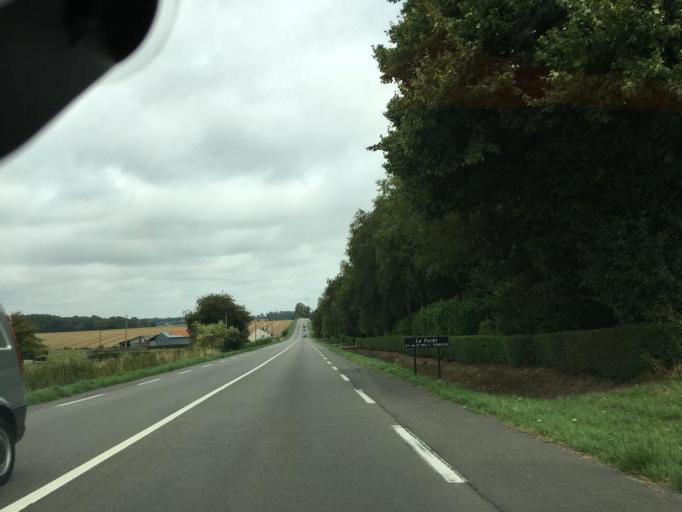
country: FR
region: Nord-Pas-de-Calais
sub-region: Departement du Pas-de-Calais
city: Saint-Pol-sur-Ternoise
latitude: 50.3996
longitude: 2.3596
